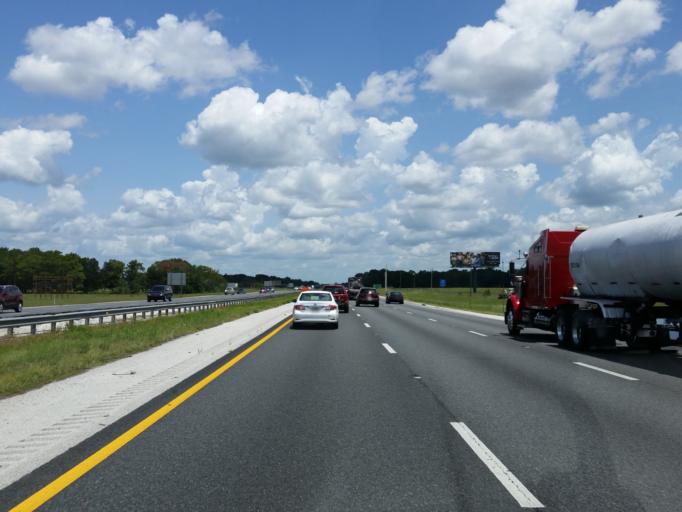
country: US
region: Florida
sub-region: Sumter County
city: Wildwood
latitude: 28.8846
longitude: -82.0946
